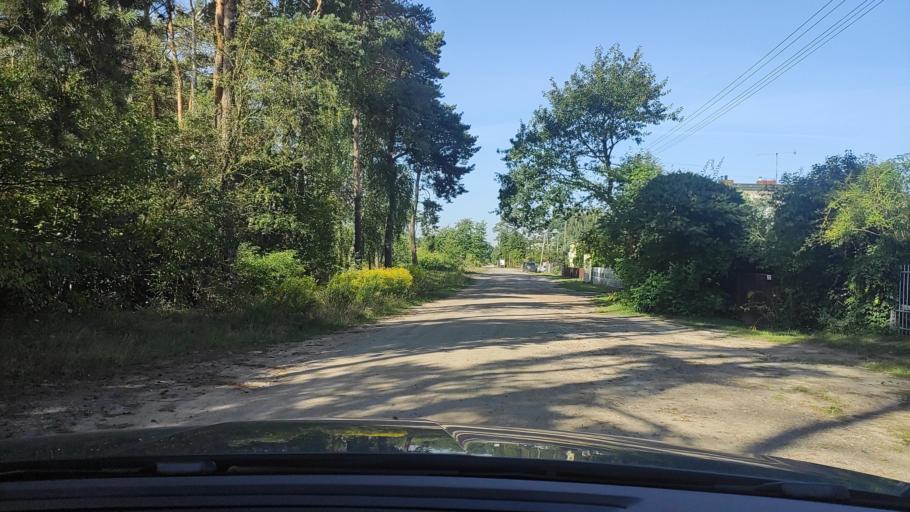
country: PL
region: Greater Poland Voivodeship
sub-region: Powiat poznanski
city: Kobylnica
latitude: 52.4294
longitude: 17.0281
